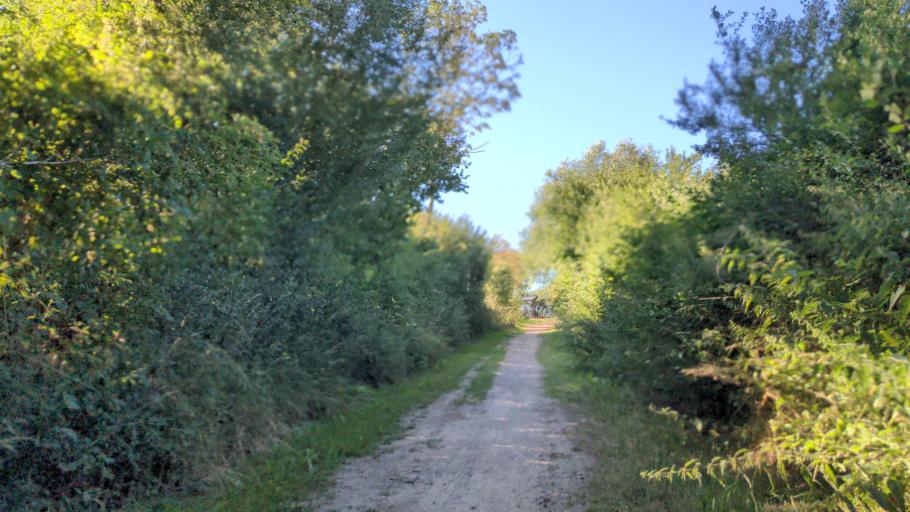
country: DE
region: Mecklenburg-Vorpommern
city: Ostseebad Boltenhagen
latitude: 53.9593
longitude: 11.2356
